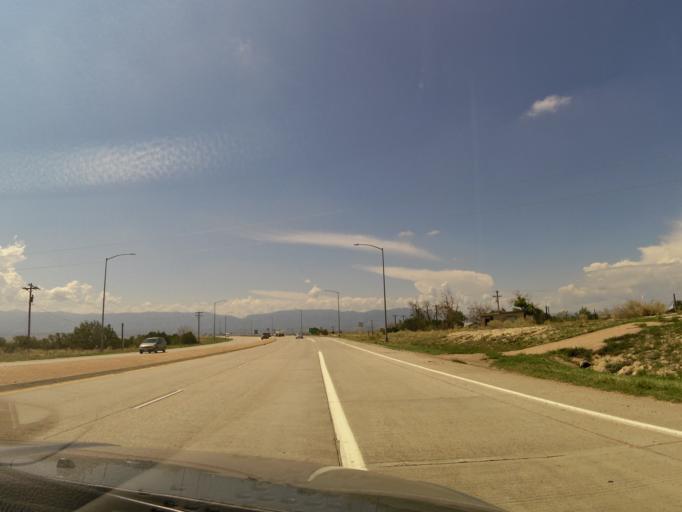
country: US
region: Colorado
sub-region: Fremont County
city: Penrose
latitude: 38.4217
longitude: -105.0366
